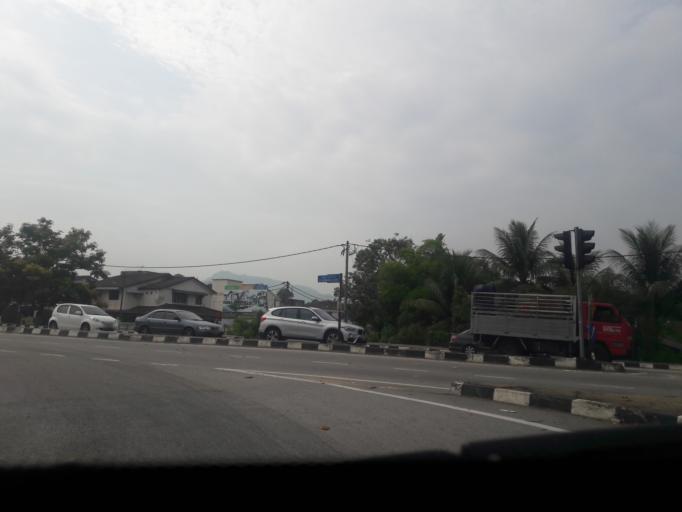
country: MY
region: Kedah
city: Kulim
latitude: 5.3528
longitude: 100.5316
